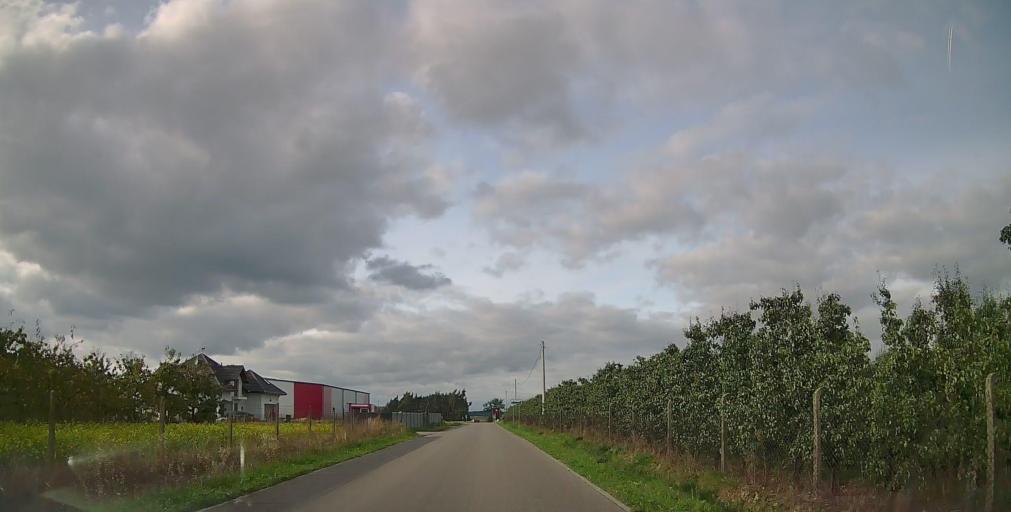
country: PL
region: Masovian Voivodeship
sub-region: Powiat bialobrzeski
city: Promna
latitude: 51.7502
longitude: 20.9624
